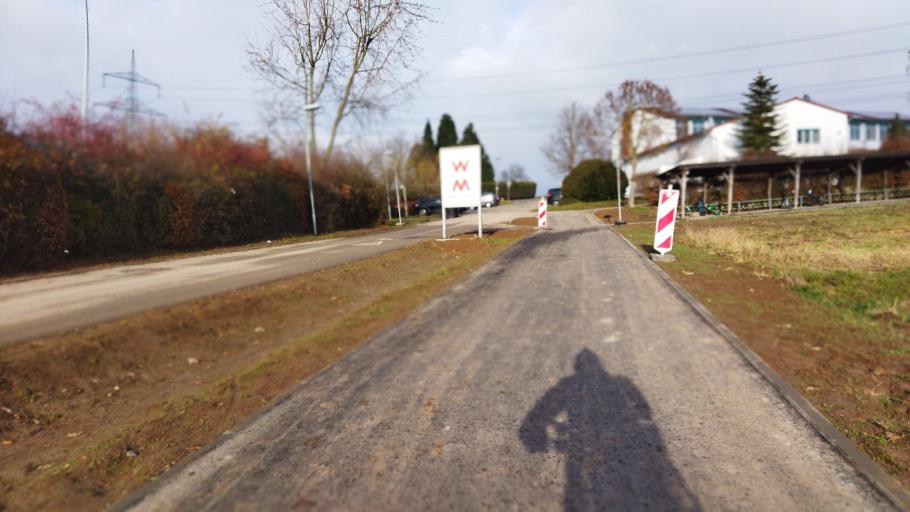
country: DE
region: Baden-Wuerttemberg
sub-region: Regierungsbezirk Stuttgart
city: Erligheim
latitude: 49.0219
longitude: 9.1045
